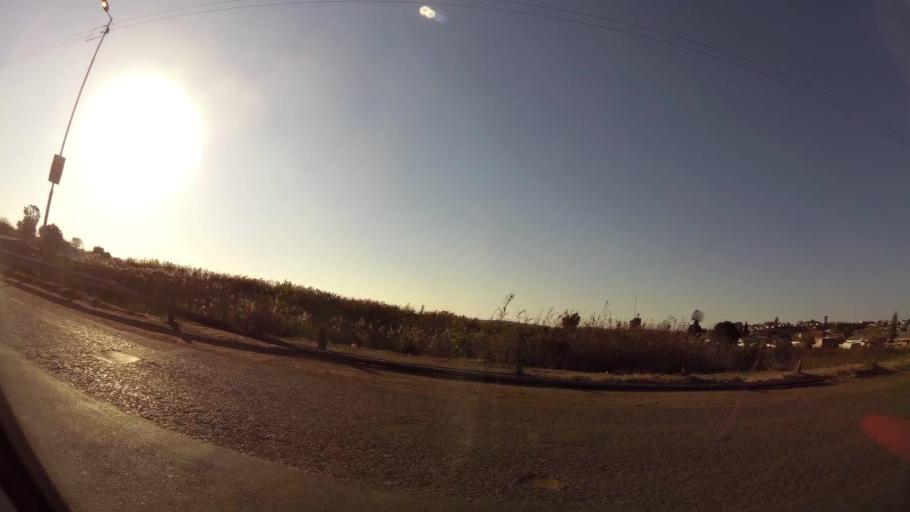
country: ZA
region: Gauteng
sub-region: City of Tshwane Metropolitan Municipality
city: Cullinan
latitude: -25.6979
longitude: 28.4026
